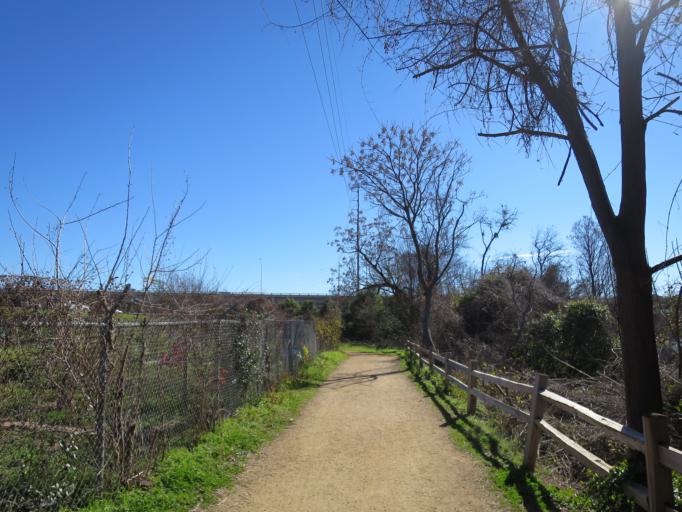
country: US
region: Texas
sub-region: Travis County
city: Rollingwood
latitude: 30.2757
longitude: -97.7725
